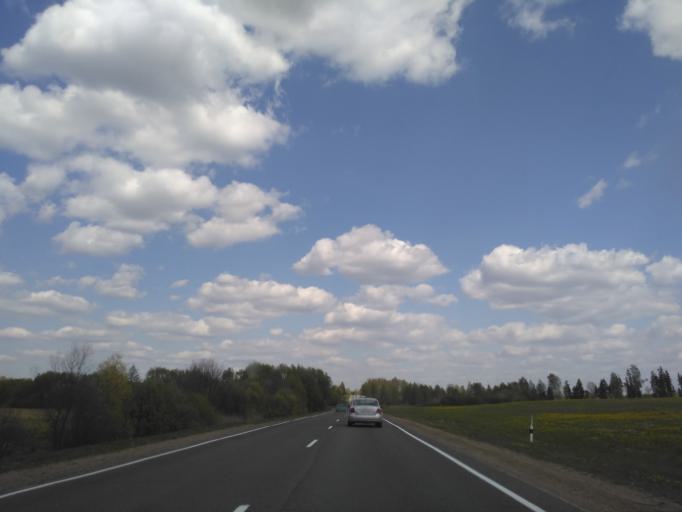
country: BY
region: Minsk
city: Vilyeyka
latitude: 54.5747
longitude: 26.8589
